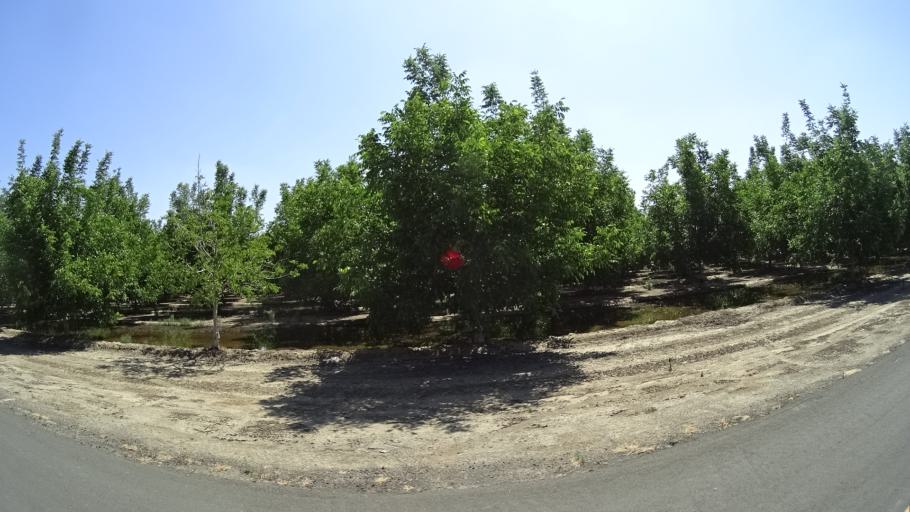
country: US
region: California
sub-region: Fresno County
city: Kingsburg
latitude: 36.4730
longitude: -119.5733
